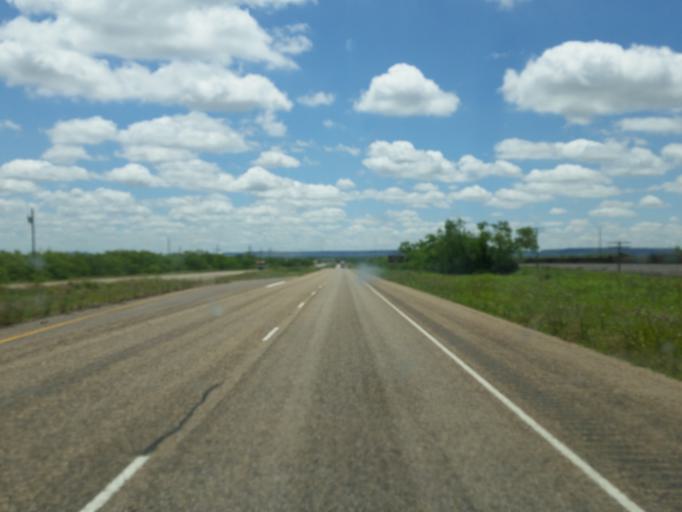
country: US
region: Texas
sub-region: Garza County
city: Post
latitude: 33.0506
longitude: -101.2093
